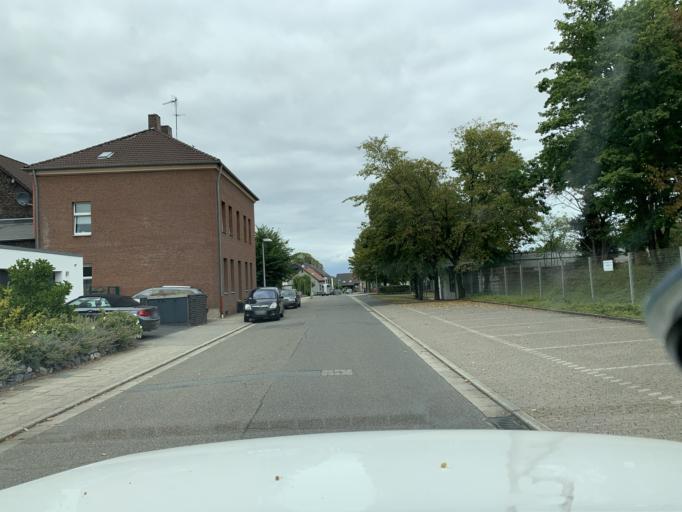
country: DE
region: North Rhine-Westphalia
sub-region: Regierungsbezirk Dusseldorf
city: Oberhausen
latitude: 51.4611
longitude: 6.9096
